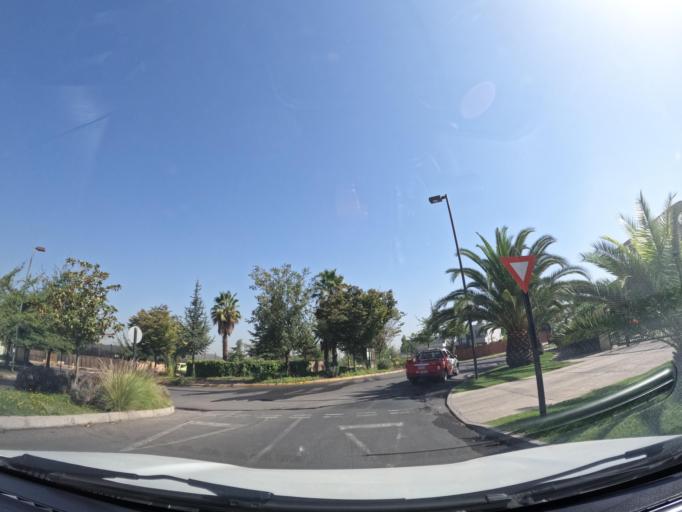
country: CL
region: Santiago Metropolitan
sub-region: Provincia de Santiago
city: Villa Presidente Frei, Nunoa, Santiago, Chile
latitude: -33.4945
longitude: -70.5563
